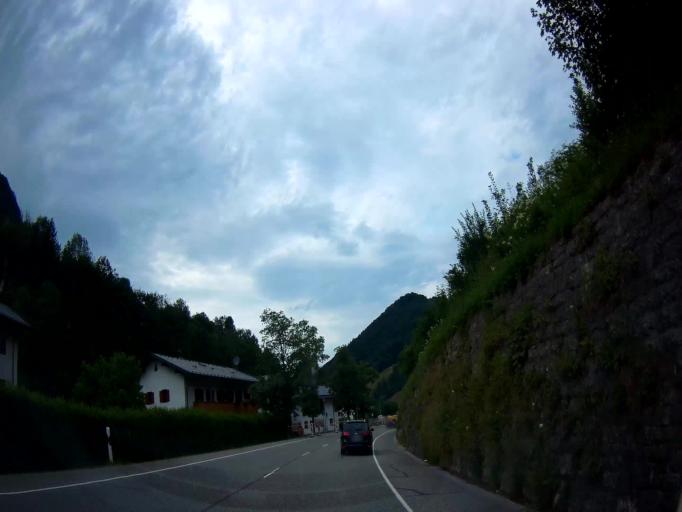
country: DE
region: Bavaria
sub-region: Upper Bavaria
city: Marktschellenberg
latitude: 47.6919
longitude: 13.0464
